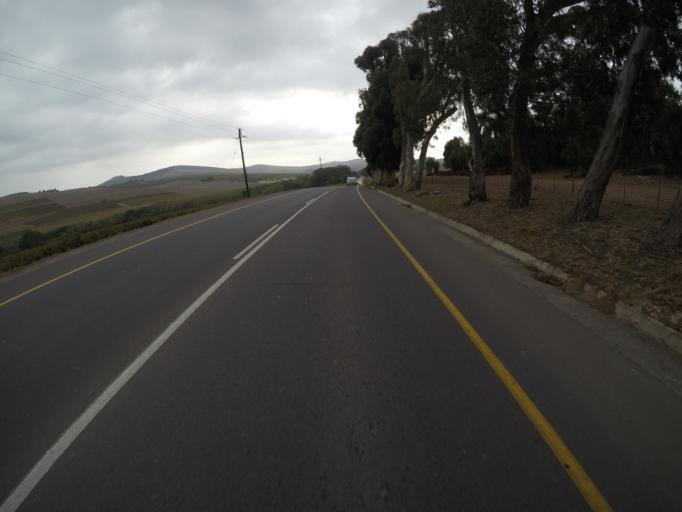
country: ZA
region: Western Cape
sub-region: City of Cape Town
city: Kraaifontein
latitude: -33.8427
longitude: 18.6206
